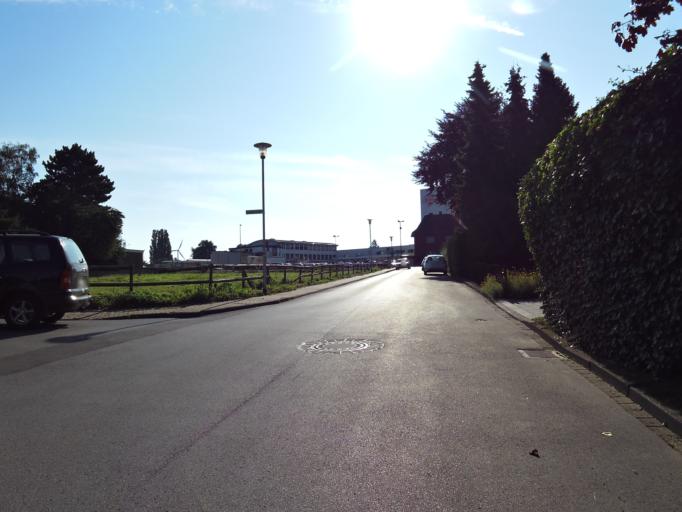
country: DE
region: North Rhine-Westphalia
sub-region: Regierungsbezirk Koln
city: Alsdorf
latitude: 50.8396
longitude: 6.1789
